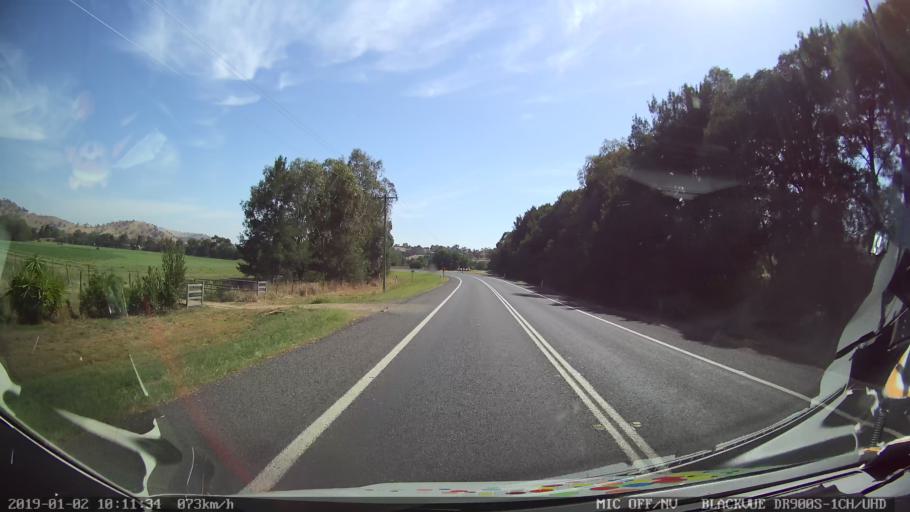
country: AU
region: New South Wales
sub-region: Gundagai
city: Gundagai
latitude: -35.0918
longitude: 148.0933
